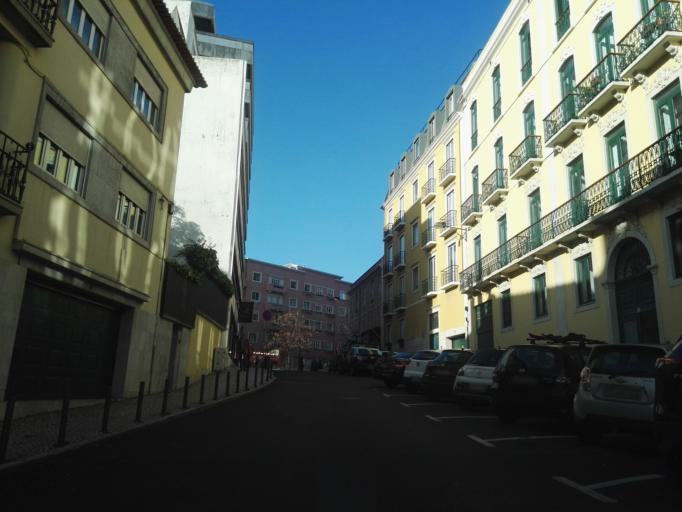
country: PT
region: Lisbon
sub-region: Lisbon
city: Lisbon
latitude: 38.7166
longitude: -9.1573
